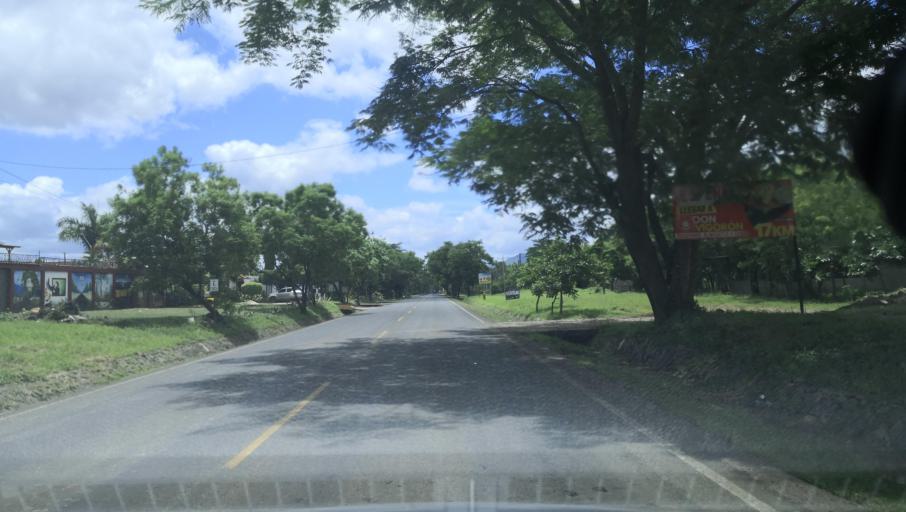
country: NI
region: Esteli
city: Esteli
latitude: 13.1655
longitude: -86.3680
